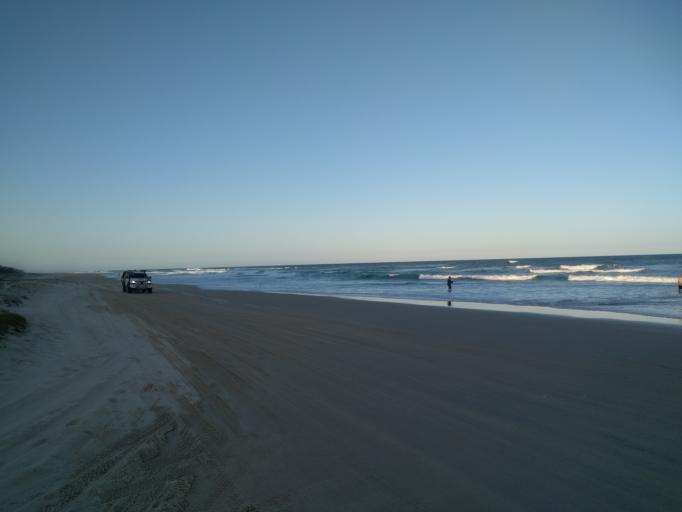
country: AU
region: Queensland
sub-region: Fraser Coast
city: Urangan
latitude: -25.4439
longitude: 153.1562
